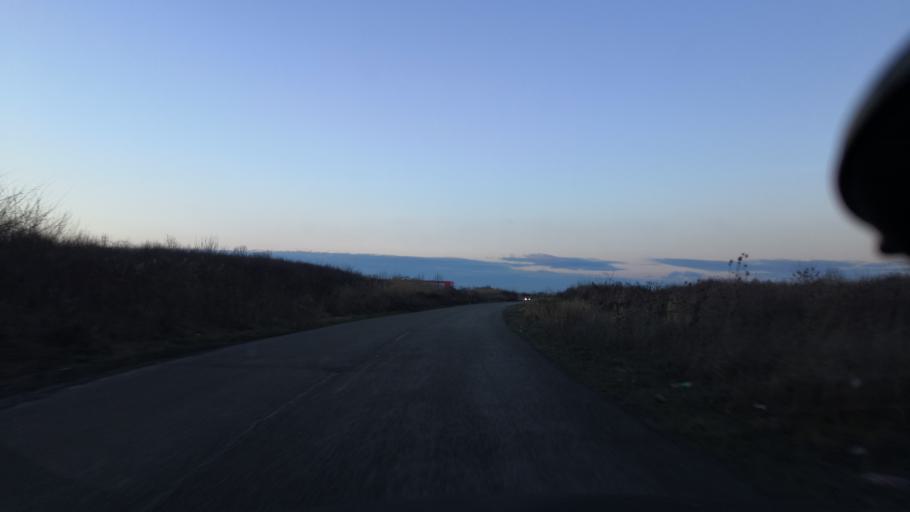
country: RS
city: Simanovci
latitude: 44.8816
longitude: 20.1183
